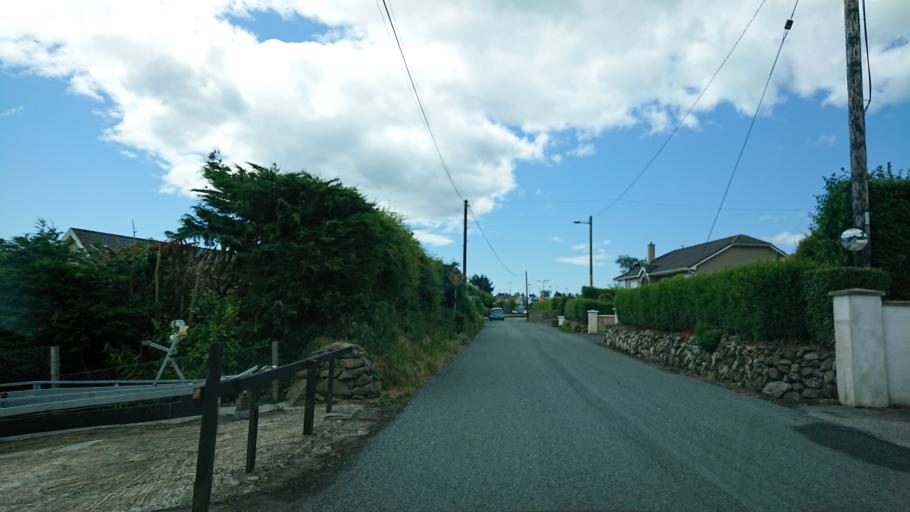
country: IE
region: Munster
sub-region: Waterford
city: Tra Mhor
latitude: 52.1742
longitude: -7.1404
